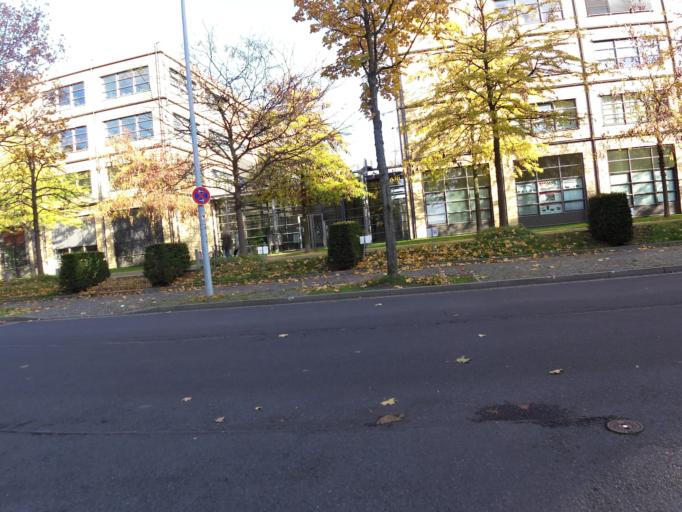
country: DE
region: Saxony
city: Leipzig
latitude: 51.3185
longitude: 12.3827
